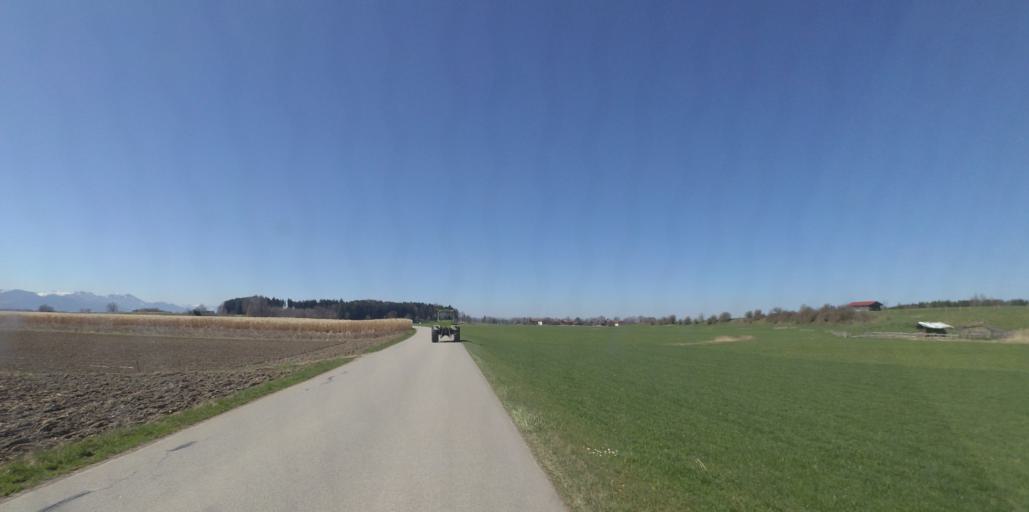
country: DE
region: Bavaria
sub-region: Upper Bavaria
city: Chieming
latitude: 47.8709
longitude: 12.5389
